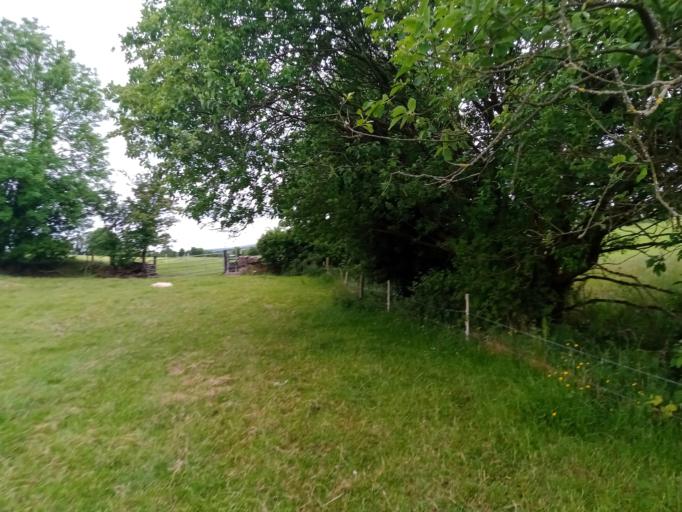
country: IE
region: Leinster
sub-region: Laois
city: Rathdowney
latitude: 52.7819
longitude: -7.4670
